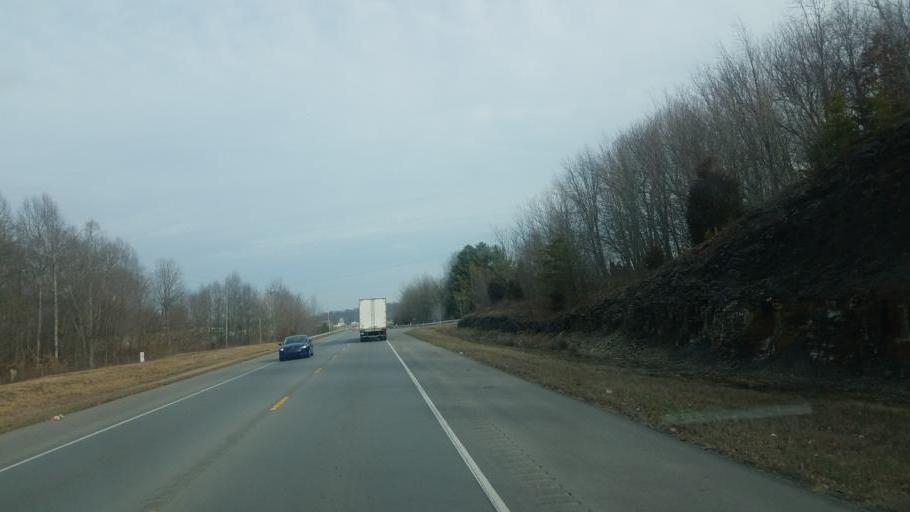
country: US
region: Kentucky
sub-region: Boyle County
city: Junction City
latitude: 37.5568
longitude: -84.7994
